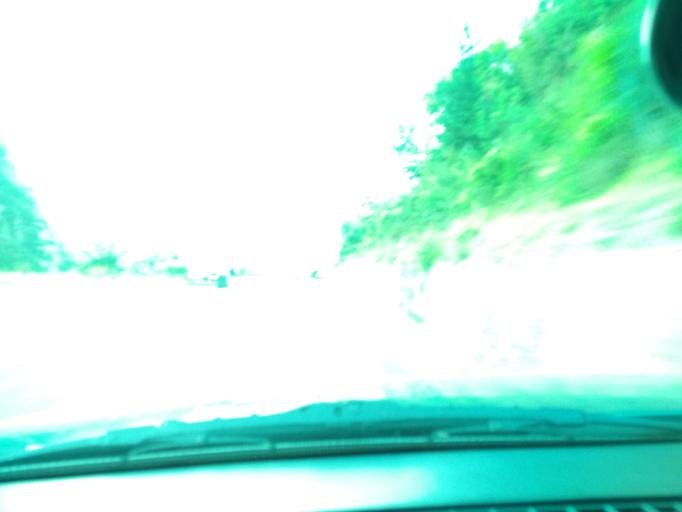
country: ME
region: Kotor
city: Kotor
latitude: 42.4054
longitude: 18.7668
